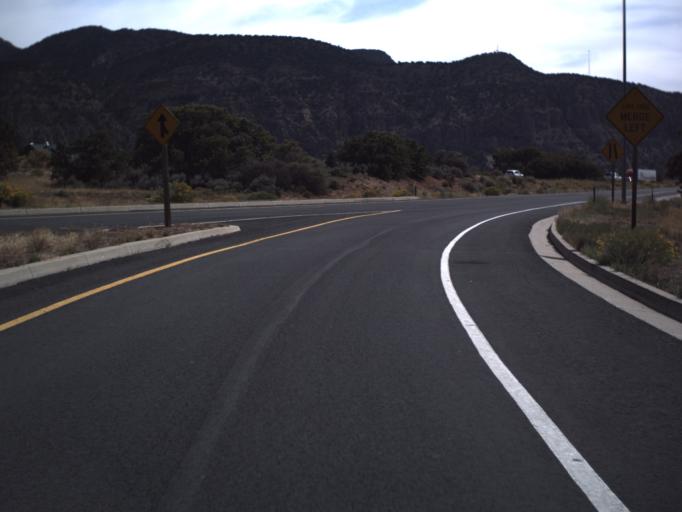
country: US
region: Utah
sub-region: Iron County
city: Cedar City
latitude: 37.5155
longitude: -113.2128
